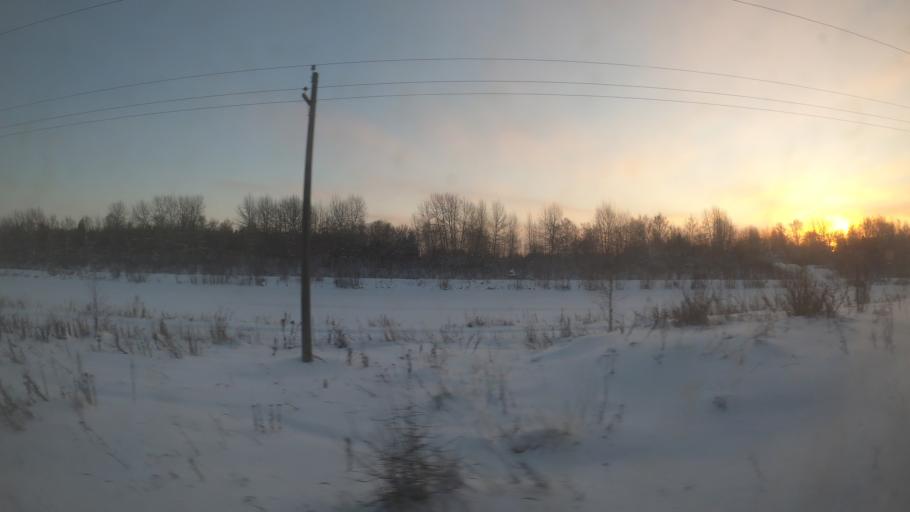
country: RU
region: Moskovskaya
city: Dedenevo
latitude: 56.2212
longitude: 37.5274
